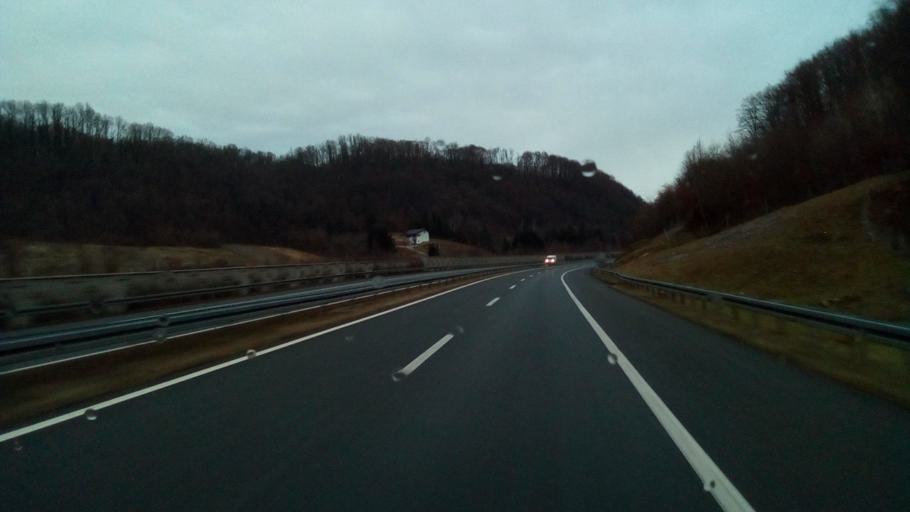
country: HR
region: Varazdinska
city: Remetinec
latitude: 46.1183
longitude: 16.2946
